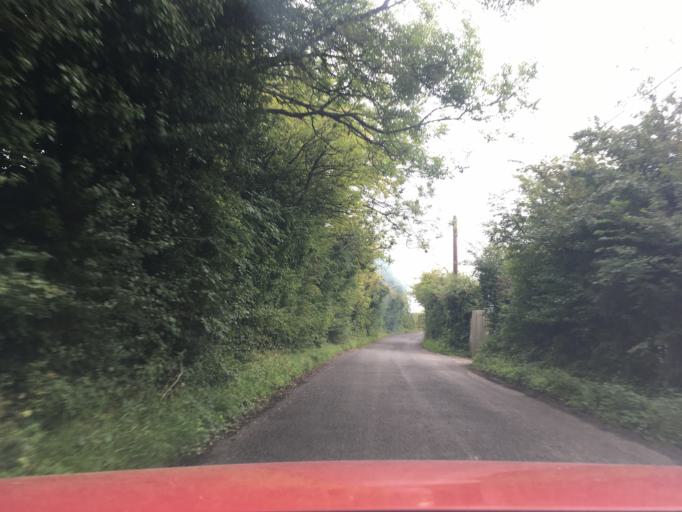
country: GB
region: England
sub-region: South Gloucestershire
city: Tytherington
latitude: 51.5970
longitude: -2.4989
